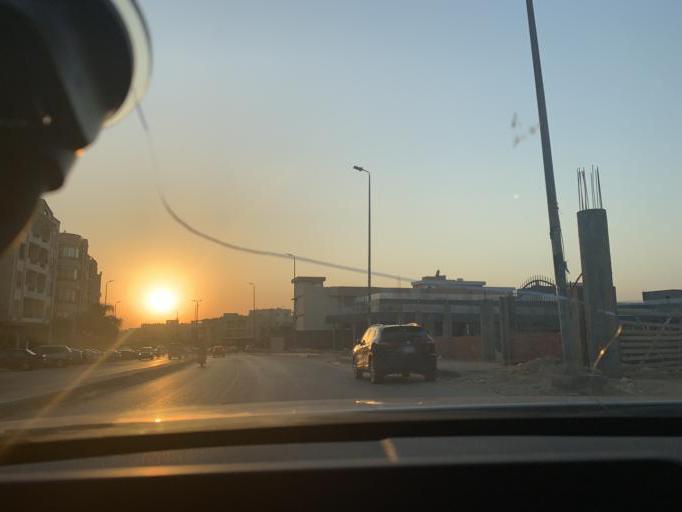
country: EG
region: Muhafazat al Qahirah
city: Cairo
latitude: 30.0054
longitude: 31.4563
